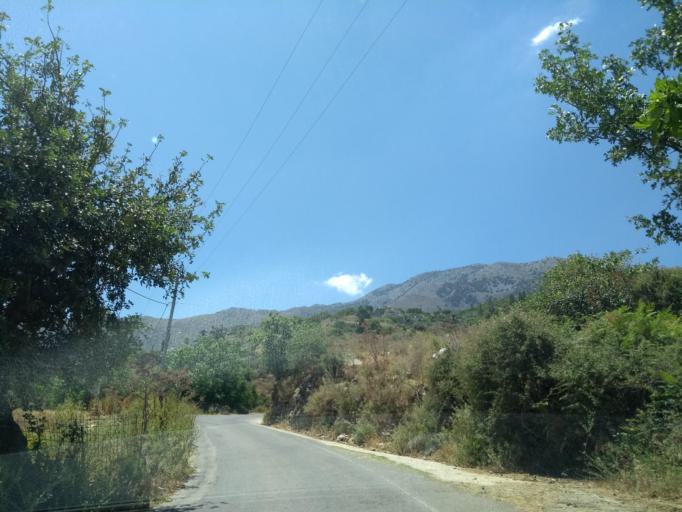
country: GR
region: Crete
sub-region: Nomos Chanias
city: Georgioupolis
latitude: 35.3178
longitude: 24.2907
